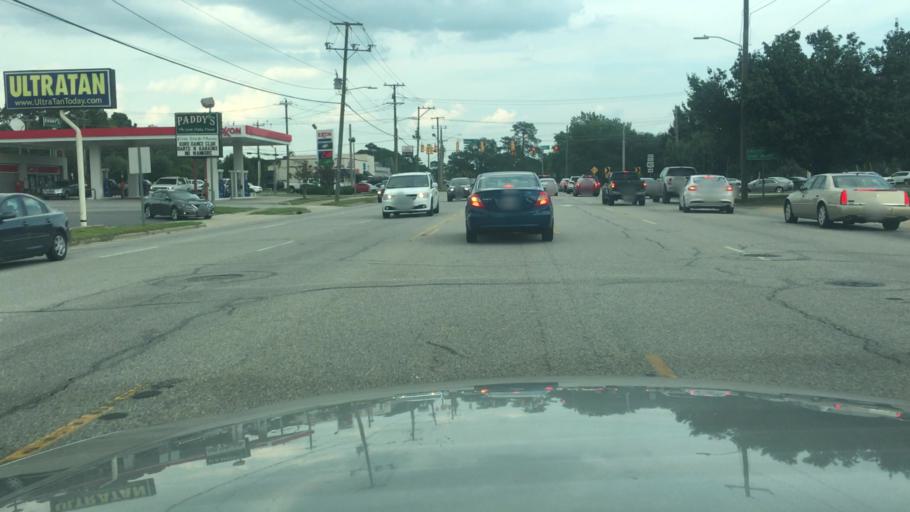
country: US
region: North Carolina
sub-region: Cumberland County
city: Fayetteville
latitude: 35.0459
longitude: -78.9205
